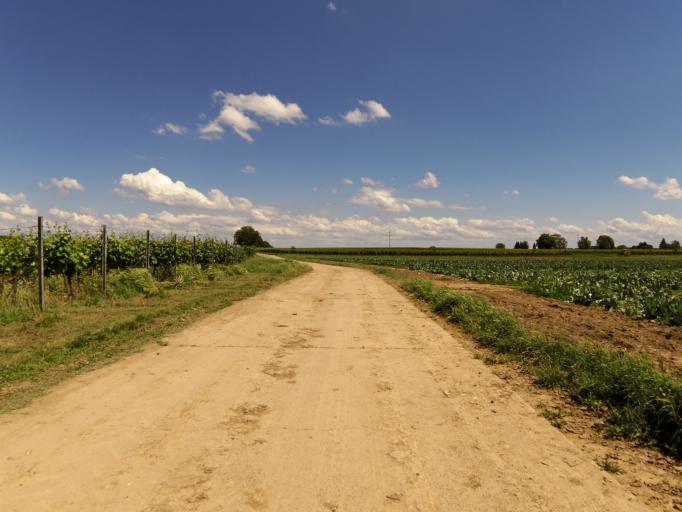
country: DE
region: Rheinland-Pfalz
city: Grossfischlingen
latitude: 49.2671
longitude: 8.1815
